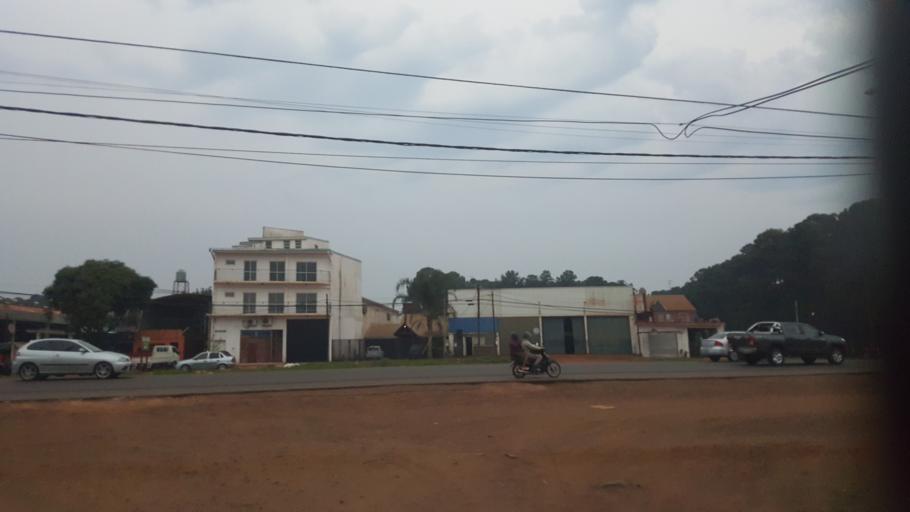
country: AR
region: Misiones
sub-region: Departamento de Capital
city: Posadas
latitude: -27.4012
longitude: -55.9299
